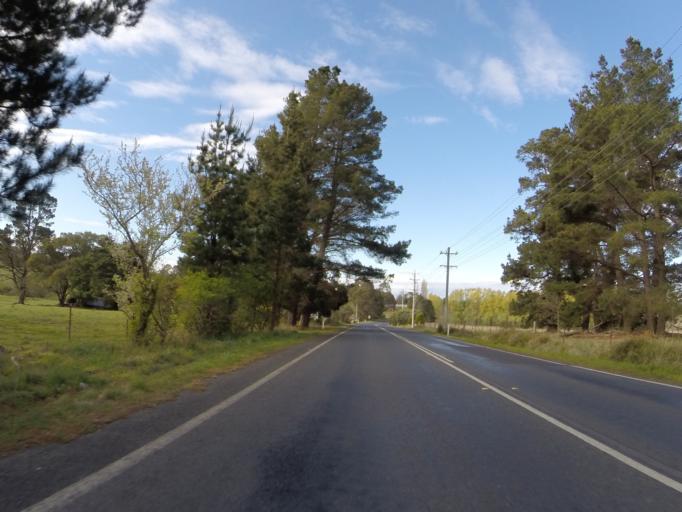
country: AU
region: New South Wales
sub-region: Wingecarribee
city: Moss Vale
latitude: -34.5738
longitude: 150.3129
